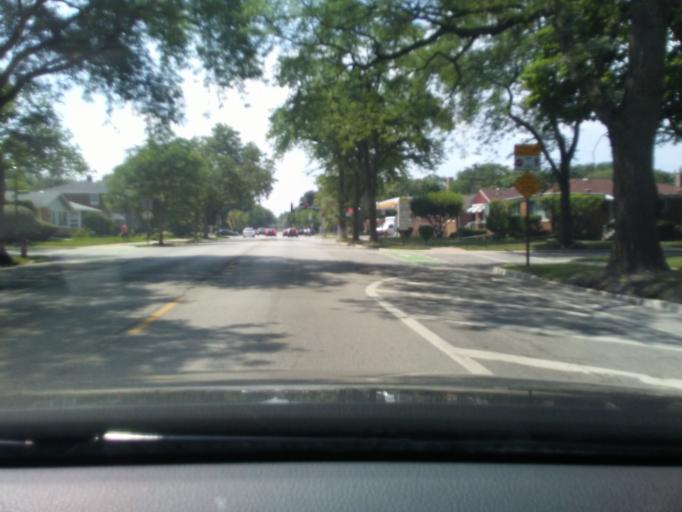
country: US
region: Illinois
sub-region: Cook County
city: Evanston
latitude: 42.0277
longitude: -87.6995
